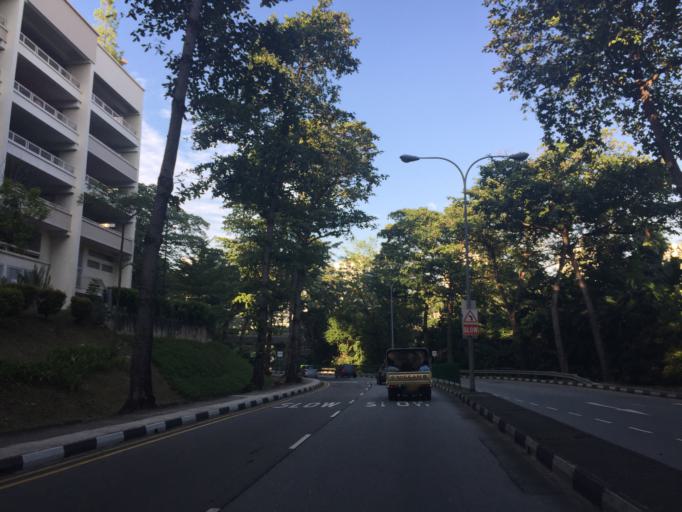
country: SG
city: Singapore
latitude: 1.3118
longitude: 103.7916
